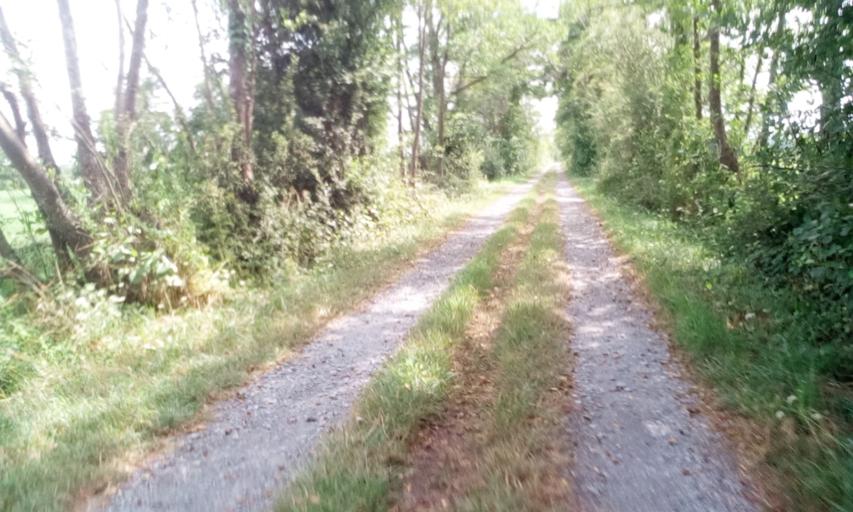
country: FR
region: Lower Normandy
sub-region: Departement du Calvados
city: Bavent
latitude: 49.2213
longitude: -0.1727
